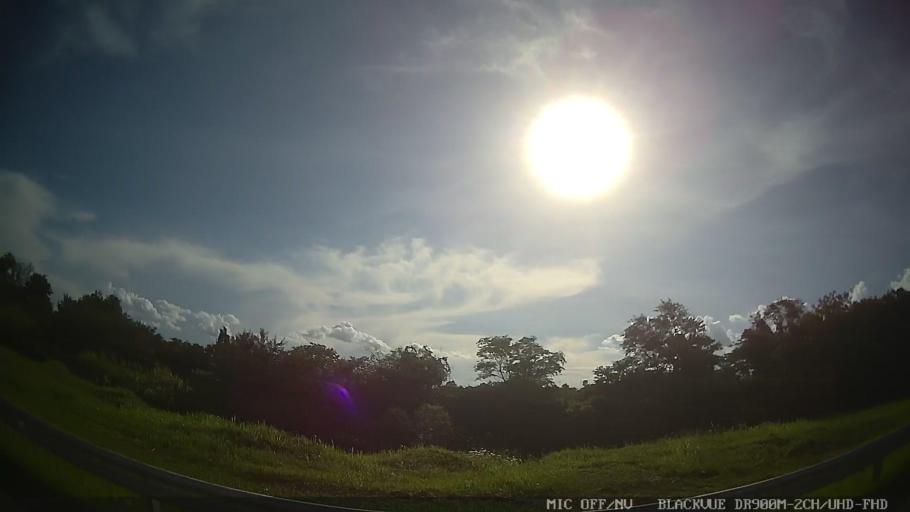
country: BR
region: Sao Paulo
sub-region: Tiete
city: Tiete
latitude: -23.1051
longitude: -47.7646
